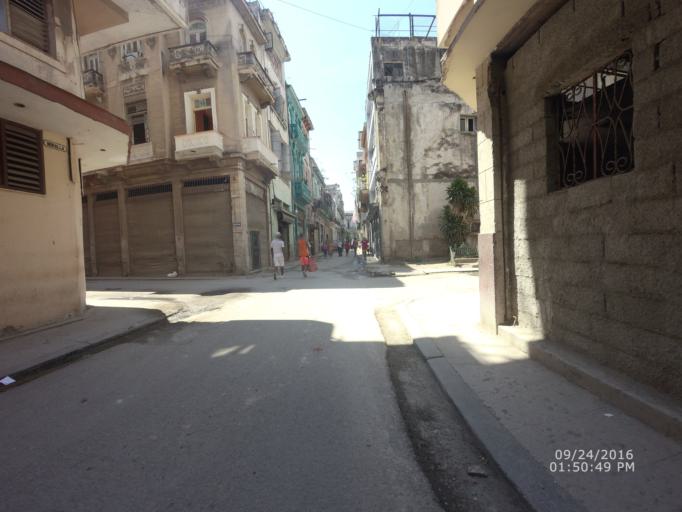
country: CU
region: La Habana
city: La Habana Vieja
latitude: 23.1344
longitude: -82.3549
